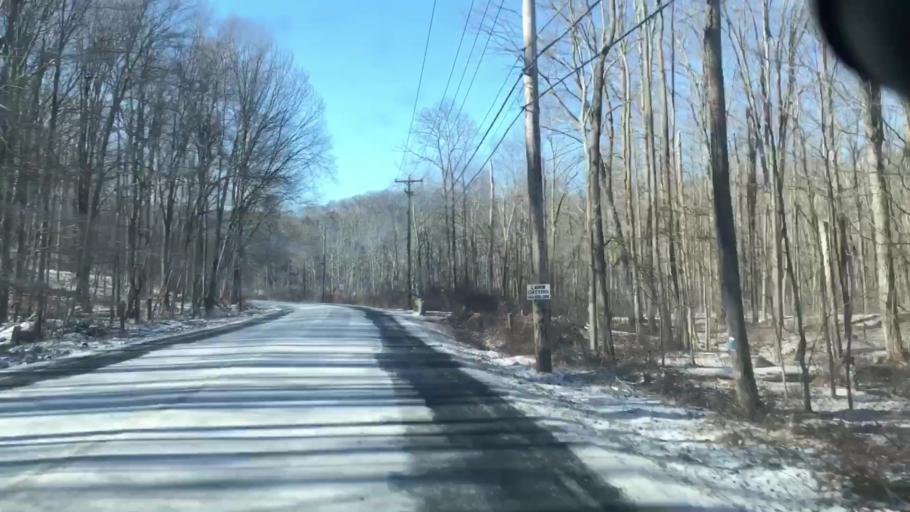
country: US
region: New York
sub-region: Putnam County
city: Carmel Hamlet
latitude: 41.3884
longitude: -73.6874
